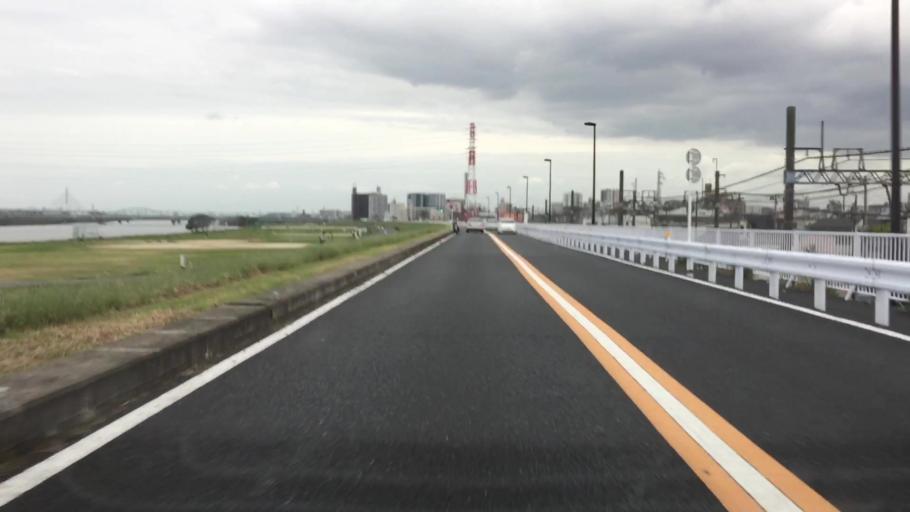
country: JP
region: Saitama
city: Soka
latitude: 35.7395
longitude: 139.8199
